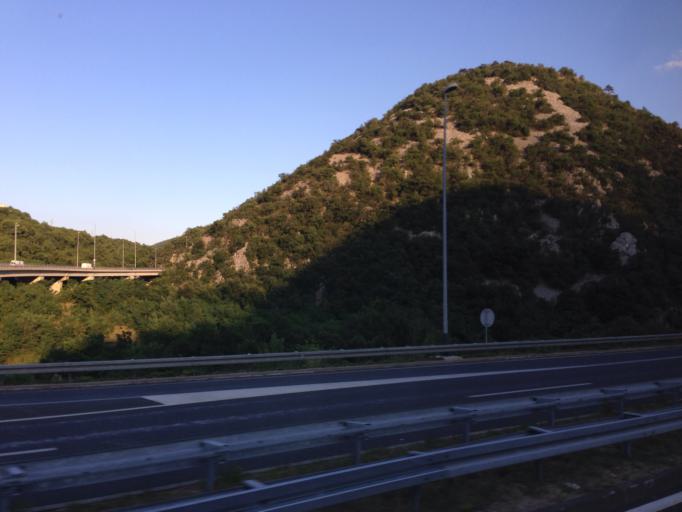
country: HR
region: Primorsko-Goranska
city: Cernik
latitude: 45.3227
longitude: 14.4922
